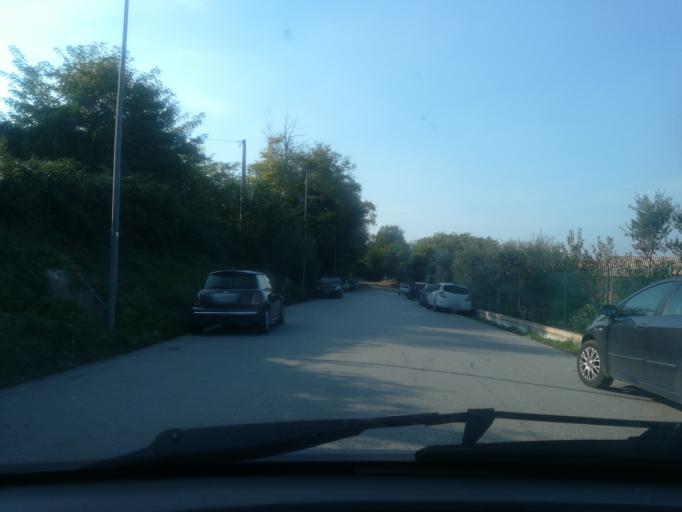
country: IT
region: The Marches
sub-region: Provincia di Macerata
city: Macerata
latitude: 43.3029
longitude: 13.4534
